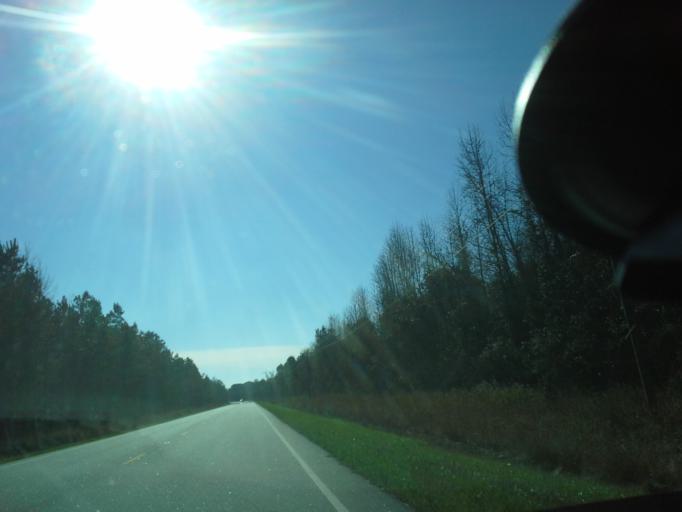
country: US
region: North Carolina
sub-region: Beaufort County
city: Belhaven
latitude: 35.5567
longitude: -76.7014
